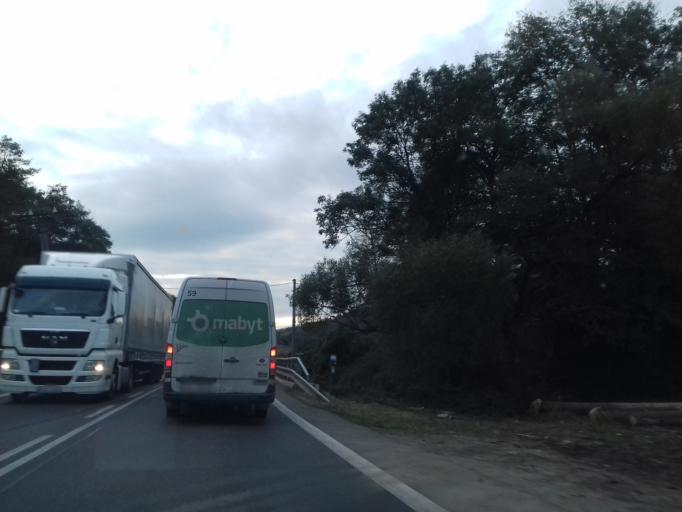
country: SK
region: Trenciansky
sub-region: Okres Trencin
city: Trencin
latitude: 48.9414
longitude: 17.9297
